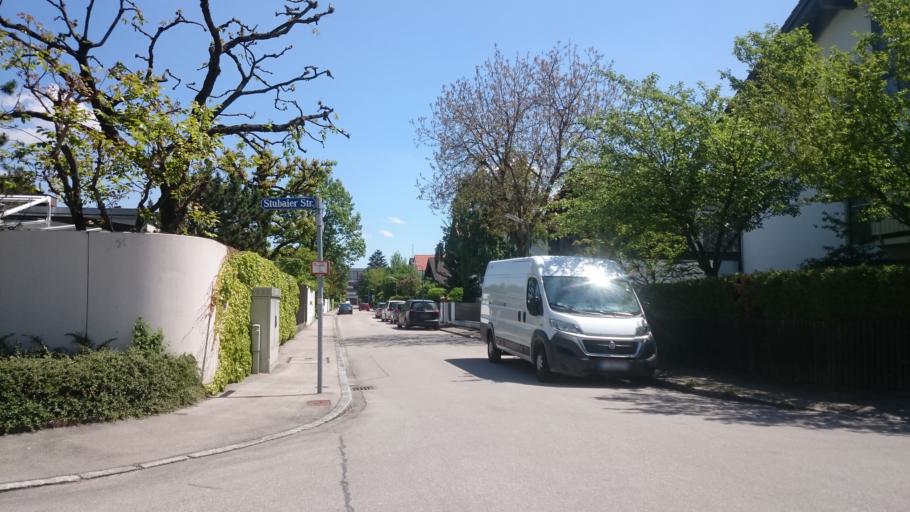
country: DE
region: Bavaria
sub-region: Upper Bavaria
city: Neubiberg
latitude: 48.0941
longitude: 11.6511
